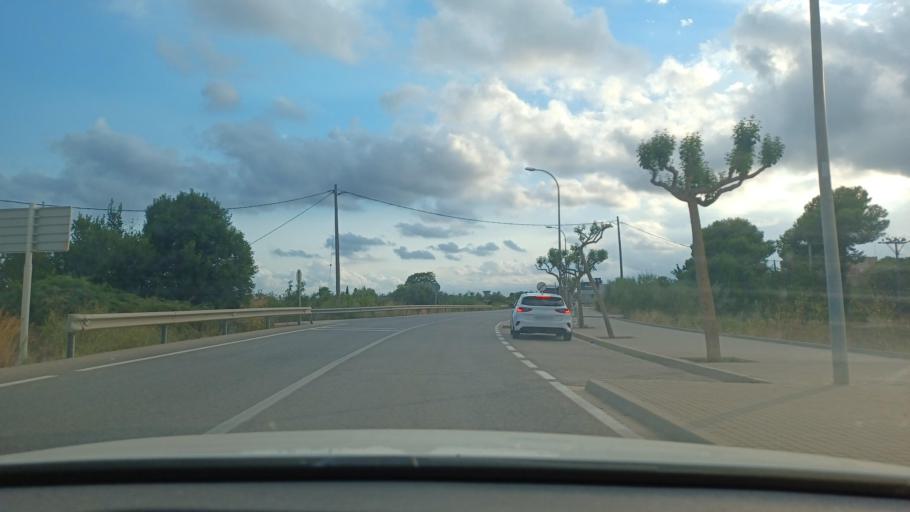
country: ES
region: Catalonia
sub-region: Provincia de Tarragona
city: Alcanar
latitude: 40.5440
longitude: 0.4897
